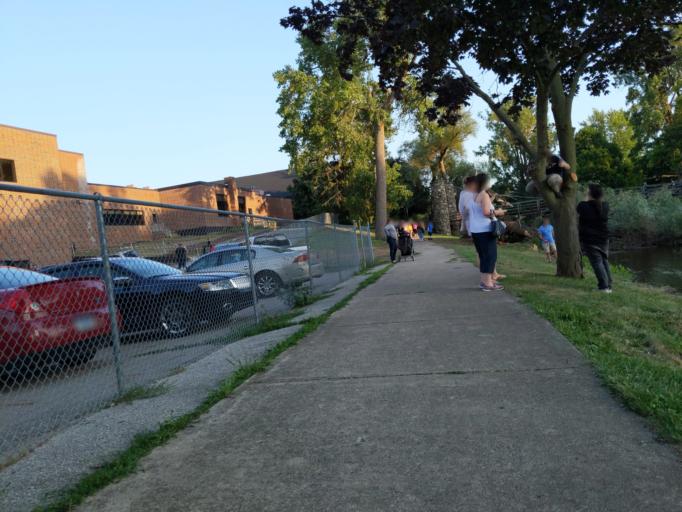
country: US
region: Michigan
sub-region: Shiawassee County
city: Owosso
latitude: 42.9996
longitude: -84.1745
